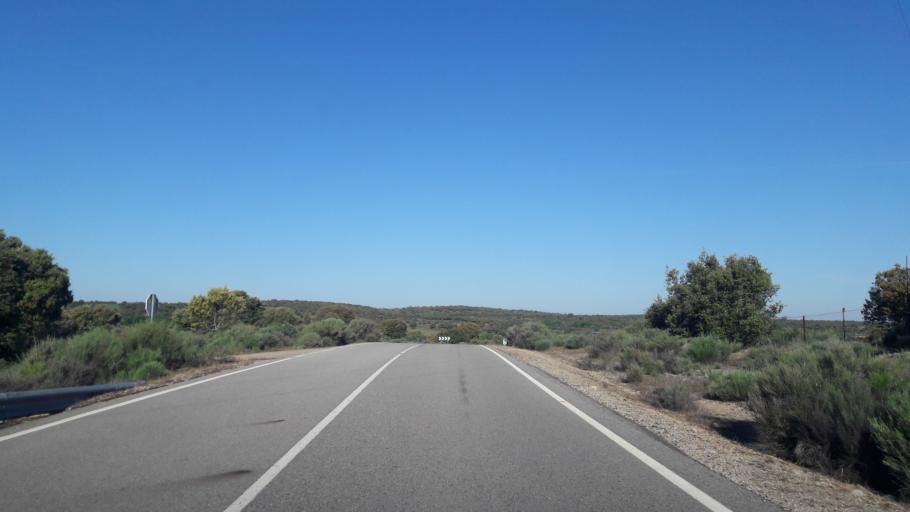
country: ES
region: Castille and Leon
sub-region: Provincia de Salamanca
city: Bogajo
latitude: 40.8899
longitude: -6.5048
